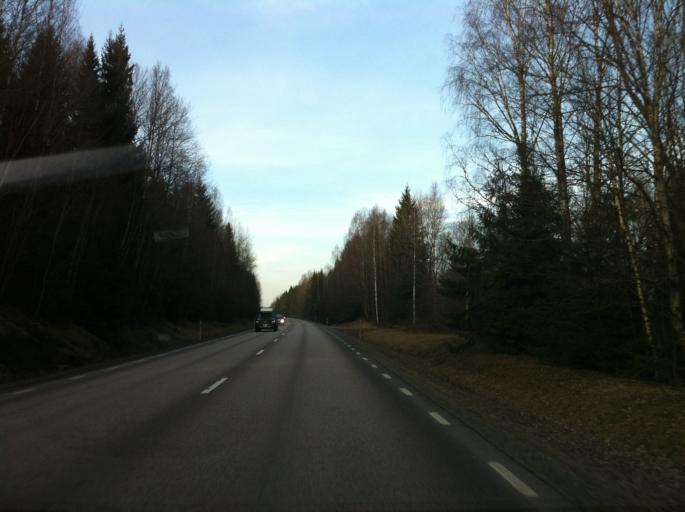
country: SE
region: Vaermland
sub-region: Storfors Kommun
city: Storfors
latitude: 59.5910
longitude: 14.2596
